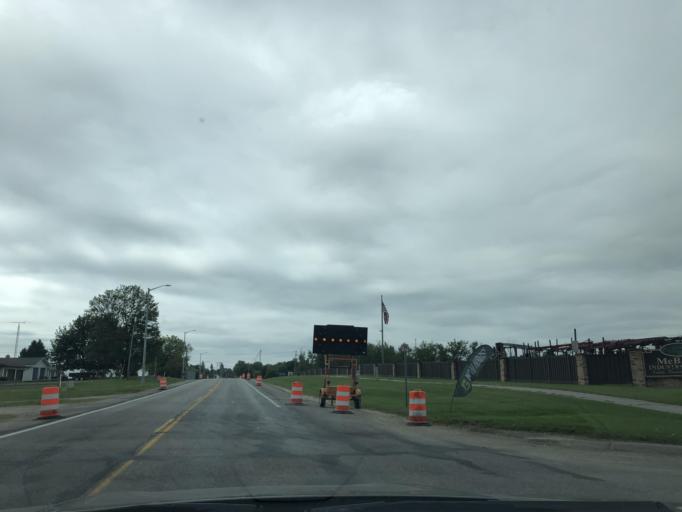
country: US
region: Michigan
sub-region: Missaukee County
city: Lake City
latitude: 44.1999
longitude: -85.2140
